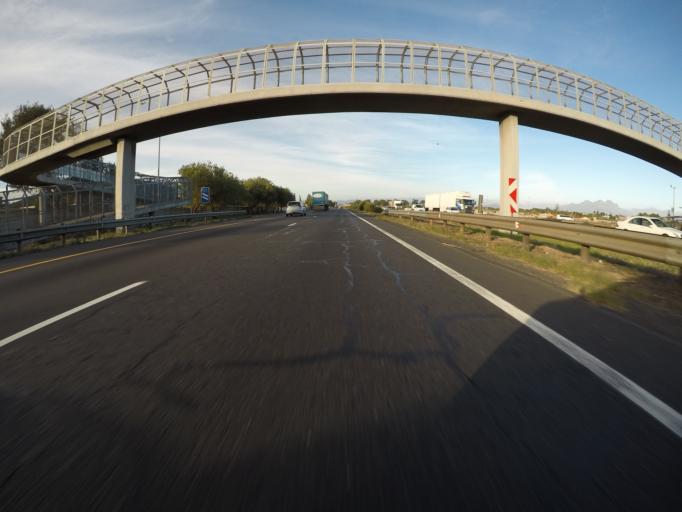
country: ZA
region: Western Cape
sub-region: City of Cape Town
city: Kraaifontein
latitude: -33.8489
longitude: 18.7093
